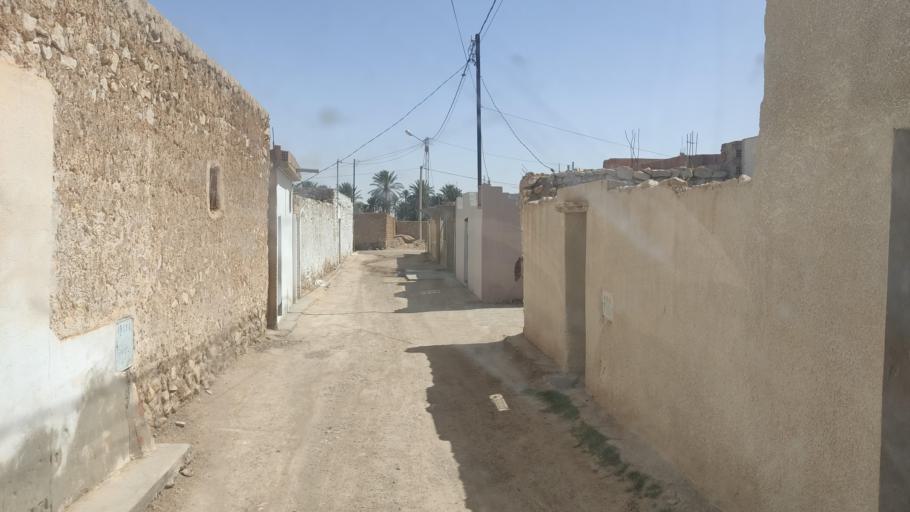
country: TN
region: Gafsa
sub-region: Gafsa Municipality
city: Gafsa
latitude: 34.3344
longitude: 8.9203
